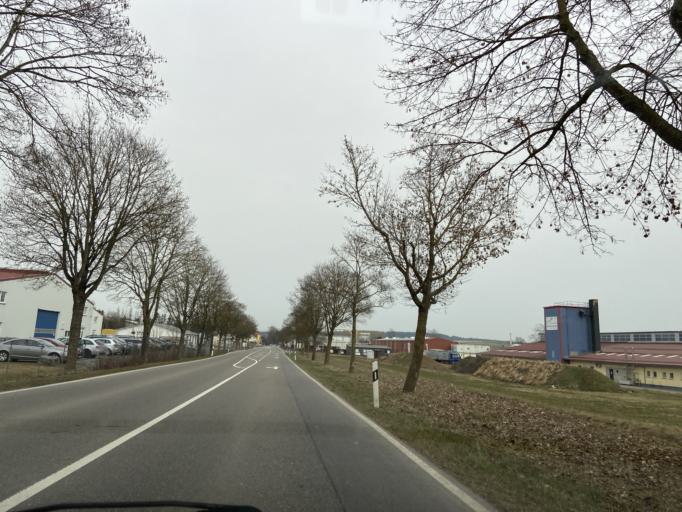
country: DE
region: Baden-Wuerttemberg
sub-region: Tuebingen Region
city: Ostrach
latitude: 47.9430
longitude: 9.3719
